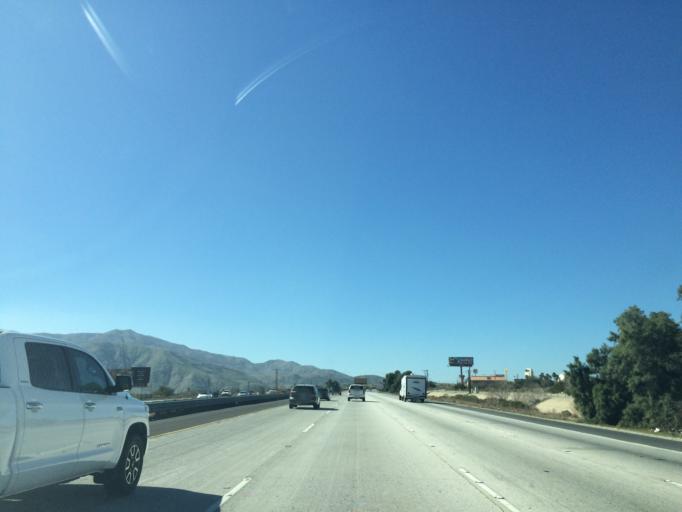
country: US
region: California
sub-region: Riverside County
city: Cabazon
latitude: 33.9196
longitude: -116.7672
